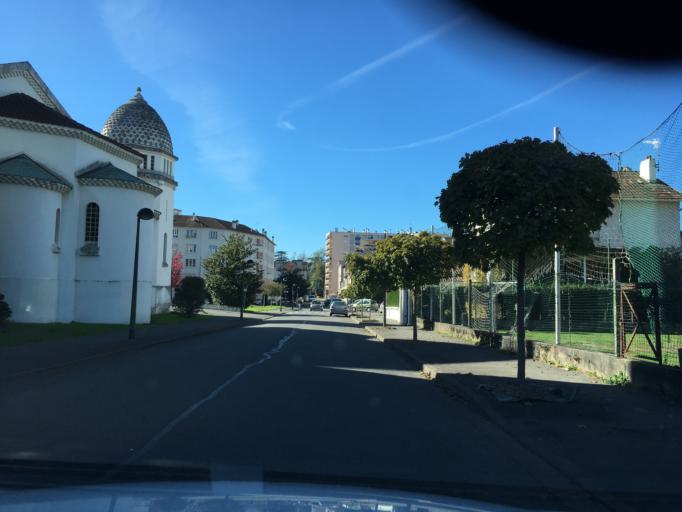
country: FR
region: Aquitaine
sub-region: Departement des Pyrenees-Atlantiques
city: Pau
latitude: 43.3066
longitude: -0.3735
